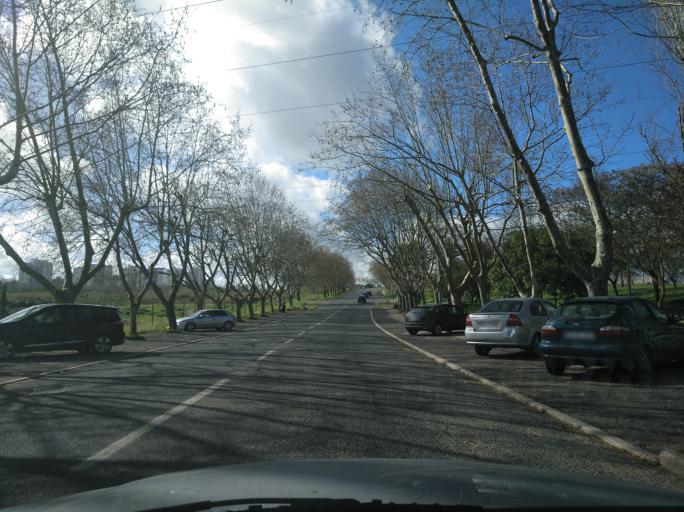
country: PT
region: Lisbon
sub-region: Odivelas
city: Povoa de Santo Adriao
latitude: 38.8142
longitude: -9.1695
